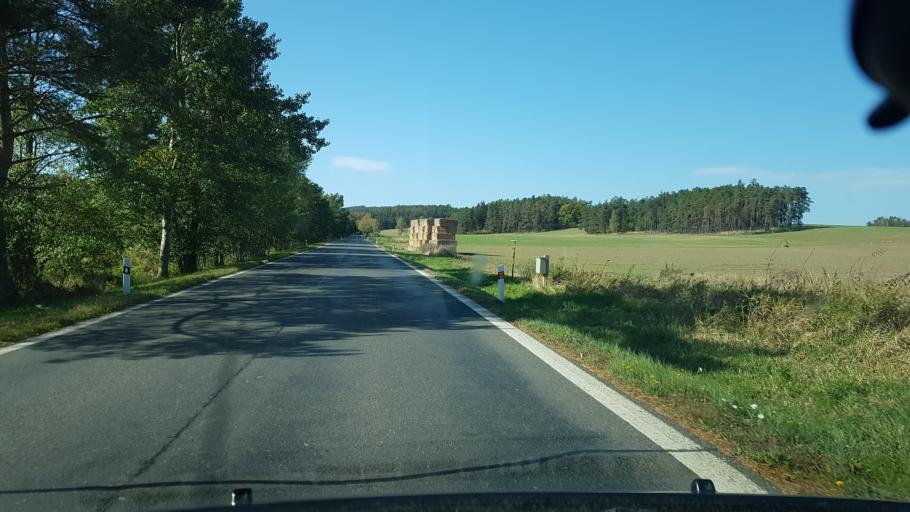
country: CZ
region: Jihocesky
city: Radomysl
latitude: 49.2956
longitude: 14.0252
